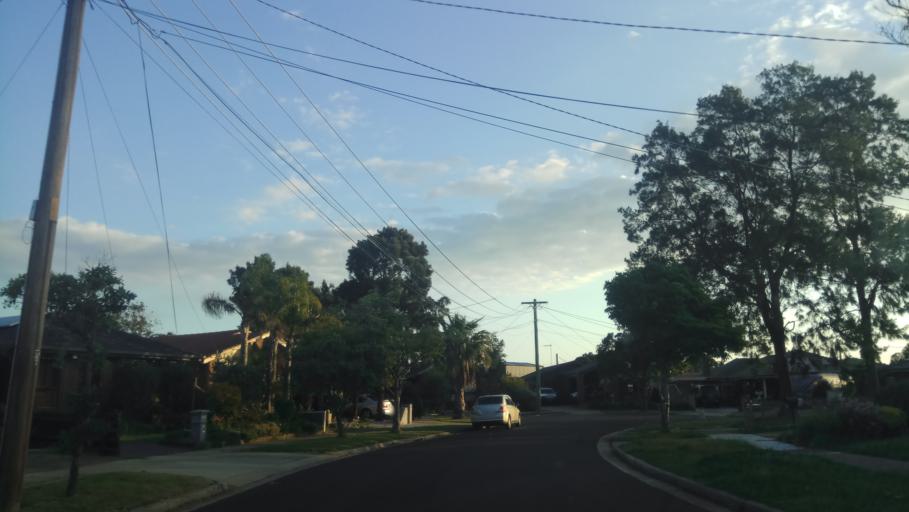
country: AU
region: Victoria
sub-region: Hobsons Bay
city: Altona Meadows
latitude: -37.8774
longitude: 144.7899
